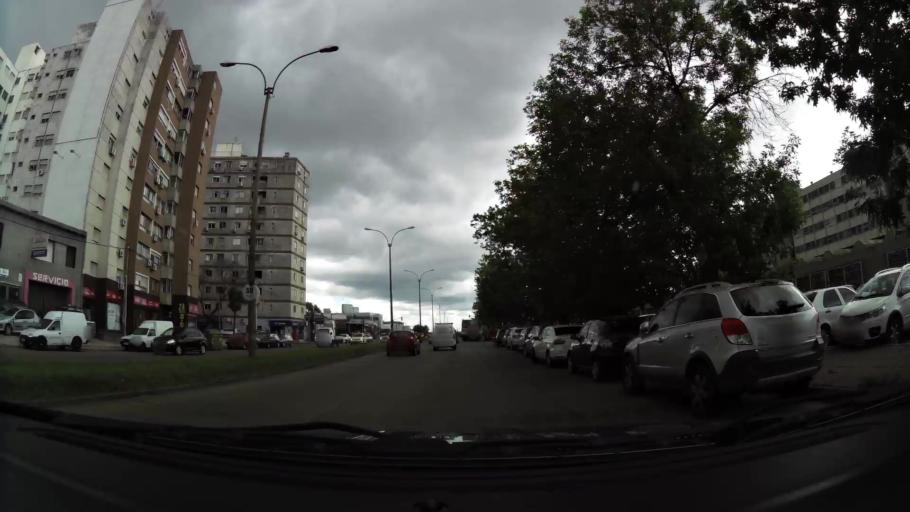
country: UY
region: Montevideo
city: Montevideo
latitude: -34.8694
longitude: -56.1607
